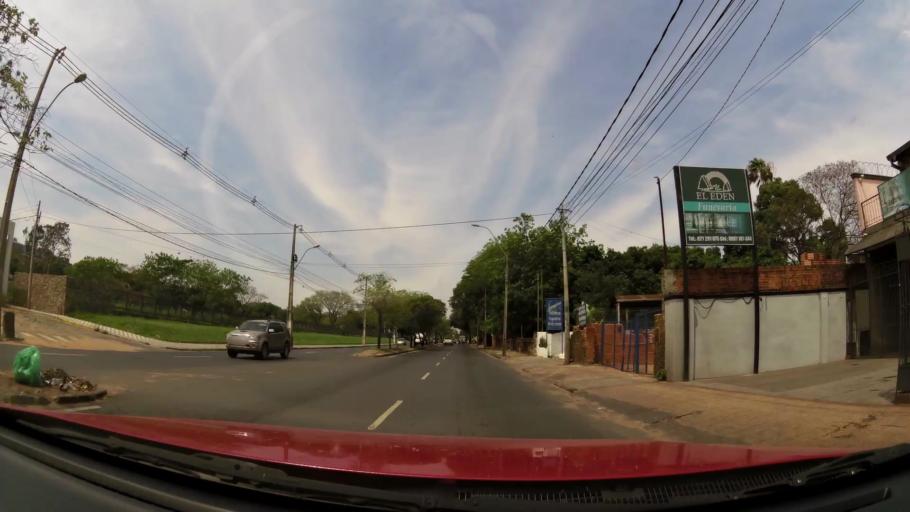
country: PY
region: Asuncion
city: Asuncion
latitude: -25.2693
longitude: -57.5836
